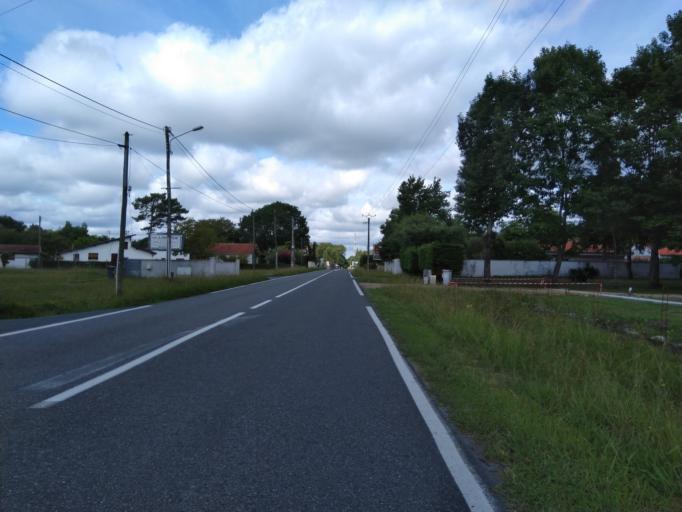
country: FR
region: Aquitaine
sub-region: Departement des Landes
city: Mees
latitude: 43.7313
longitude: -1.0974
